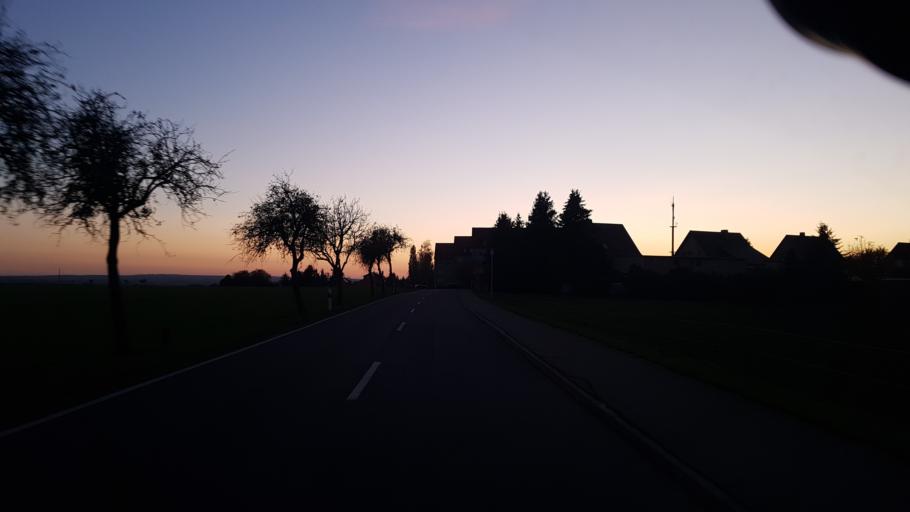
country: DE
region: Saxony
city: Arzberg
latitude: 51.5302
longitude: 13.1337
